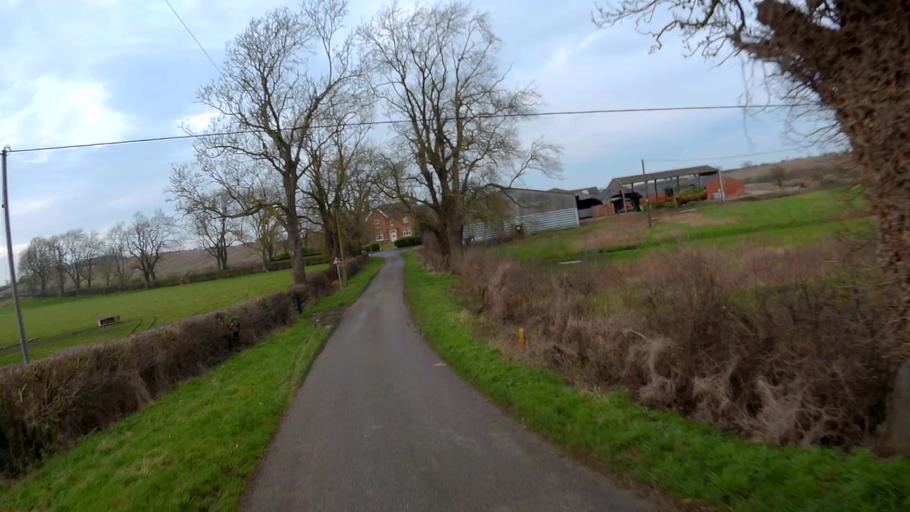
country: GB
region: England
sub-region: Lincolnshire
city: Bourne
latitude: 52.8268
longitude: -0.4609
